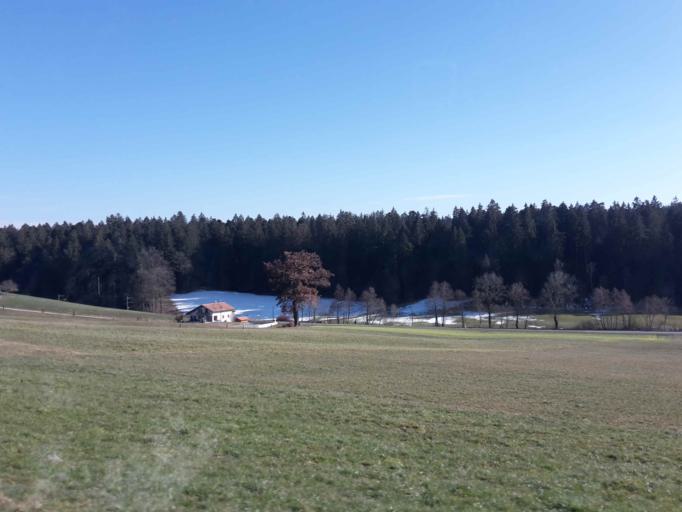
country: CH
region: Bern
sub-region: Emmental District
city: Durrenroth
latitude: 47.0914
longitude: 7.7699
